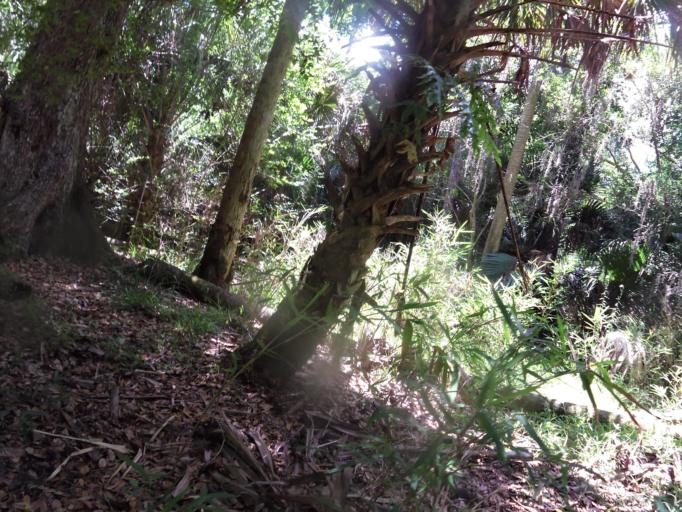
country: US
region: Florida
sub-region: Flagler County
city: Flagler Beach
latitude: 29.4202
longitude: -81.1397
